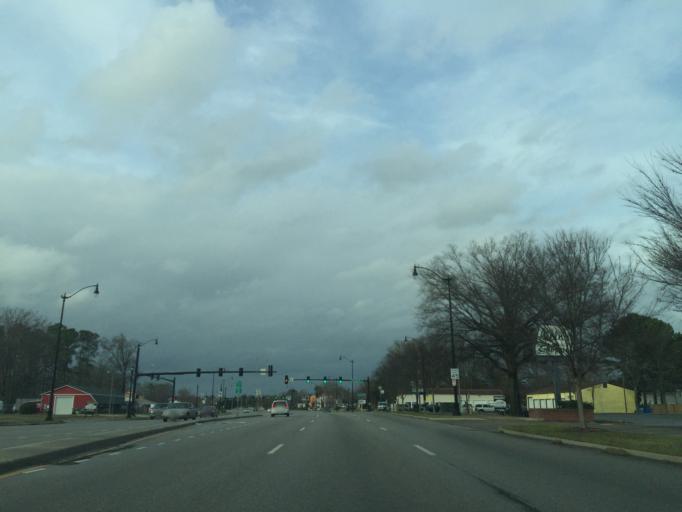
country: US
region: Virginia
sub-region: City of Newport News
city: Newport News
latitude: 37.0822
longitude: -76.4977
